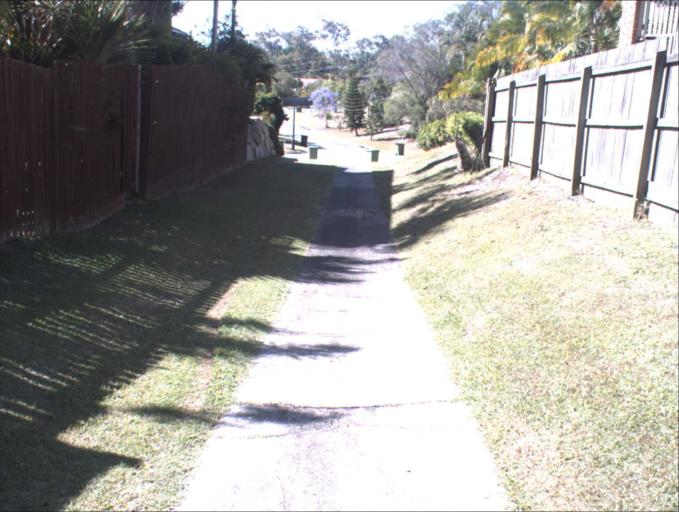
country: AU
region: Queensland
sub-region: Logan
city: Windaroo
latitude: -27.7274
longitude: 153.1863
